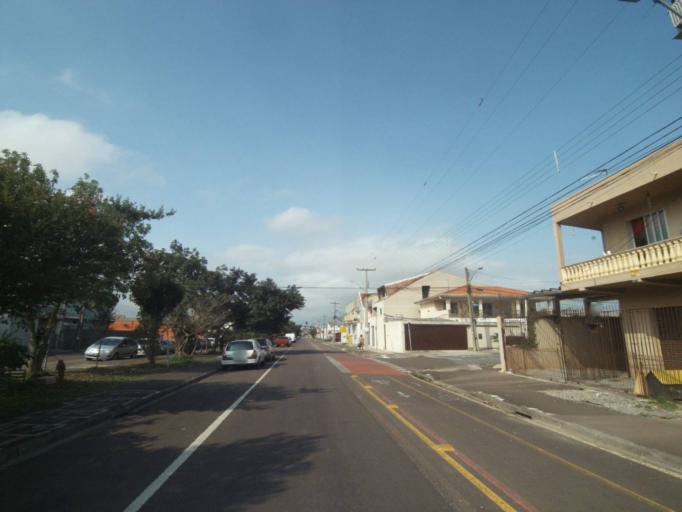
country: BR
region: Parana
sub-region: Sao Jose Dos Pinhais
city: Sao Jose dos Pinhais
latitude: -25.5398
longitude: -49.2600
